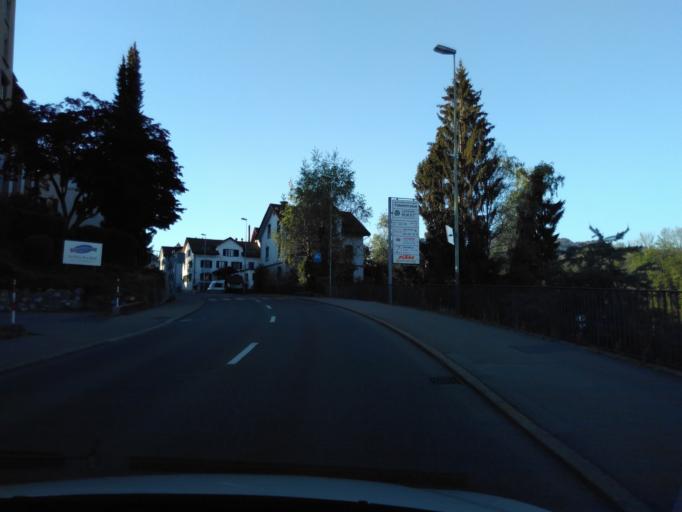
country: CH
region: Zurich
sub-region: Bezirk Hinwil
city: Tann / Tann (Dorfkern)
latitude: 47.2630
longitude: 8.8517
